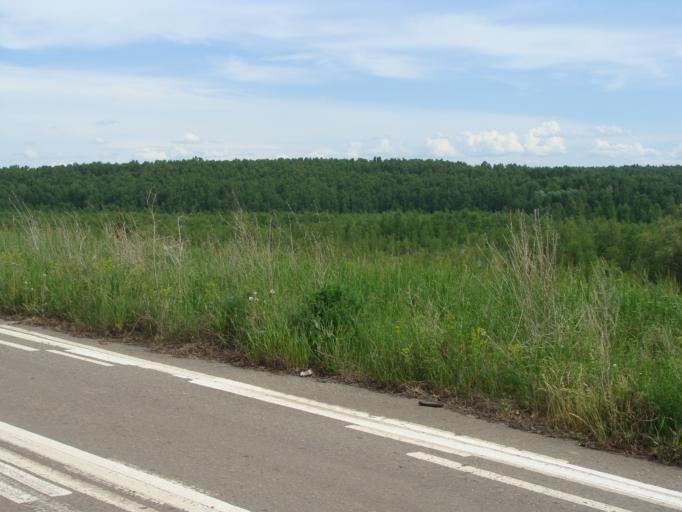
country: RU
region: Altai Krai
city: Sannikovo
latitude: 53.3559
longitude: 83.9998
